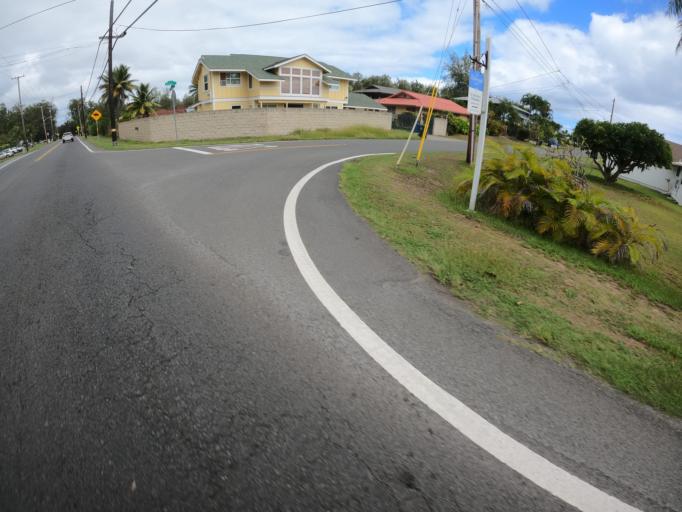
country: US
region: Hawaii
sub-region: Honolulu County
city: Waimanalo Beach
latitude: 21.3390
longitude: -157.7030
